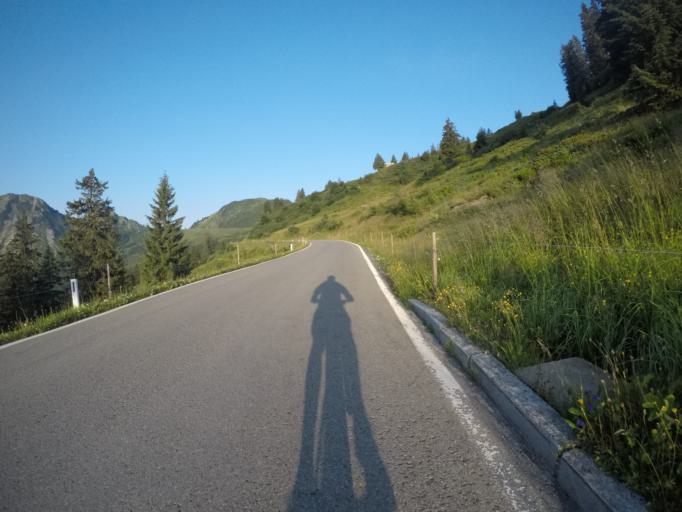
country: AT
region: Vorarlberg
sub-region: Politischer Bezirk Bregenz
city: Damuels
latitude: 47.2771
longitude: 9.8473
